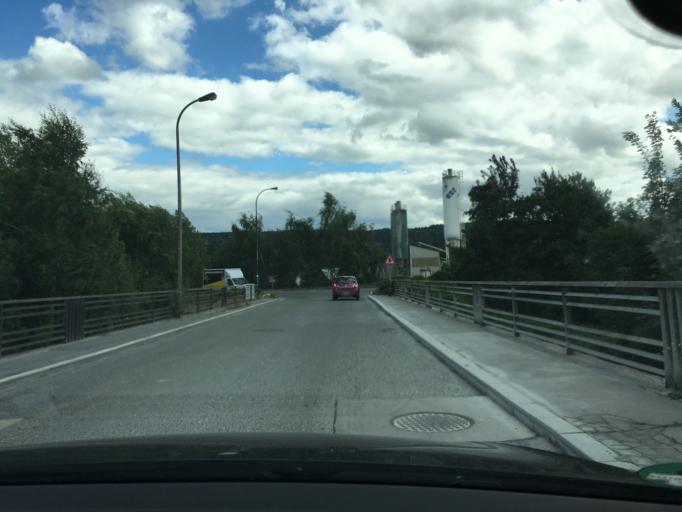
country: BE
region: Wallonia
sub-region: Province de Liege
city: Engis
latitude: 50.5633
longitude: 5.3553
